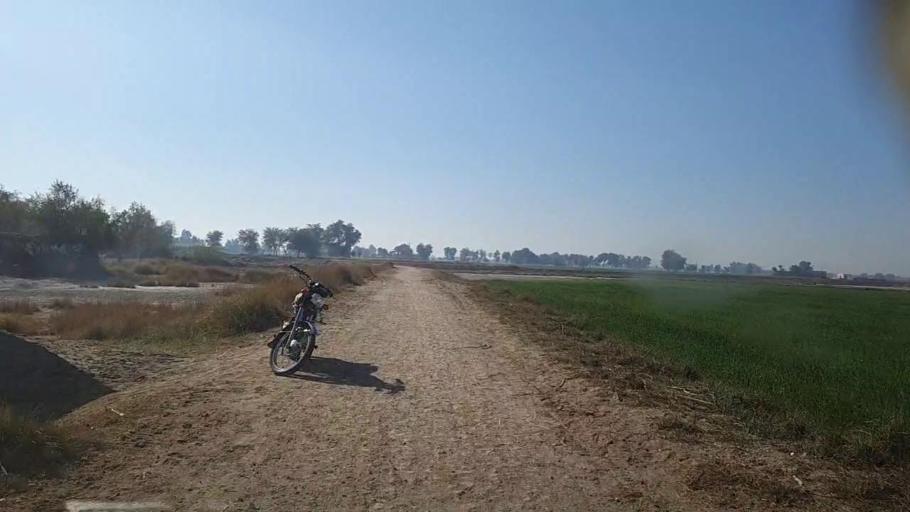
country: PK
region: Sindh
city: Khairpur
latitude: 28.0035
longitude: 69.6474
